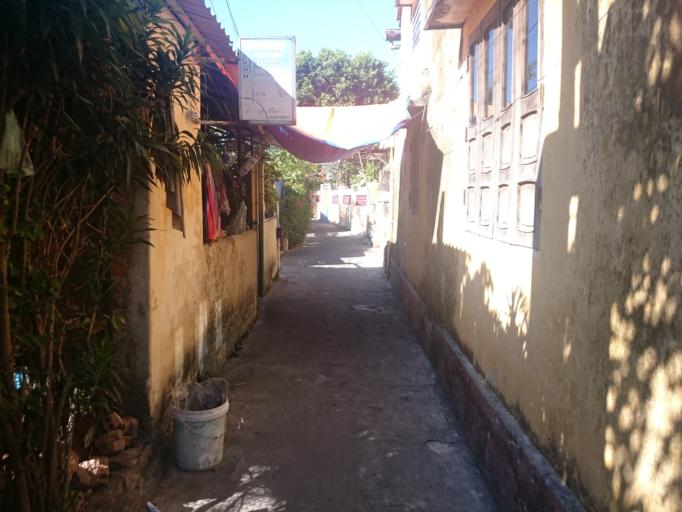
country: VN
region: Quang Nam
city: Hoi An
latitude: 15.8777
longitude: 108.3305
